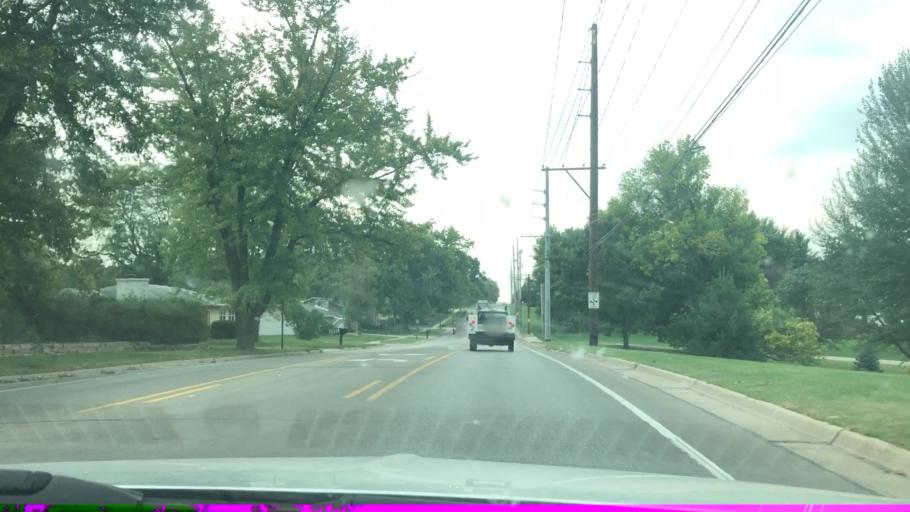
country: US
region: Iowa
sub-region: Marshall County
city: Marshalltown
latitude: 42.0238
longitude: -92.9222
